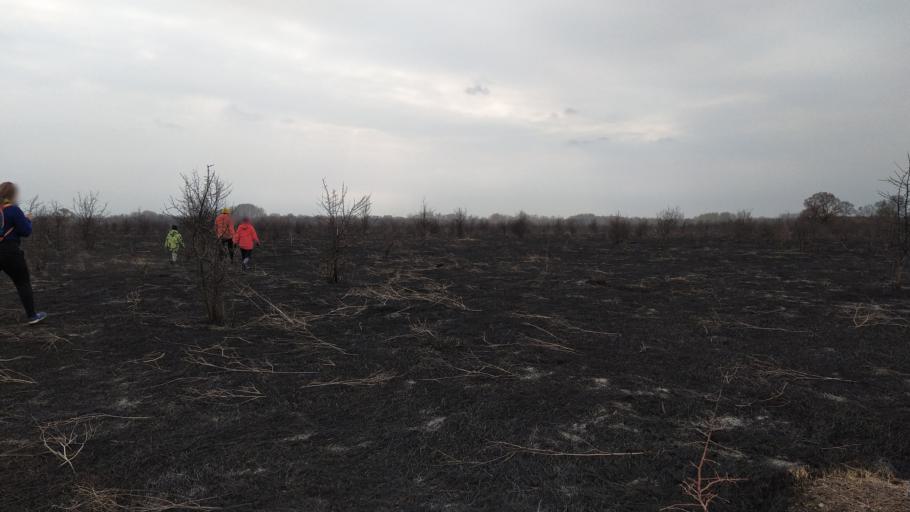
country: RU
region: Rostov
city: Semikarakorsk
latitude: 47.5477
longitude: 40.6818
